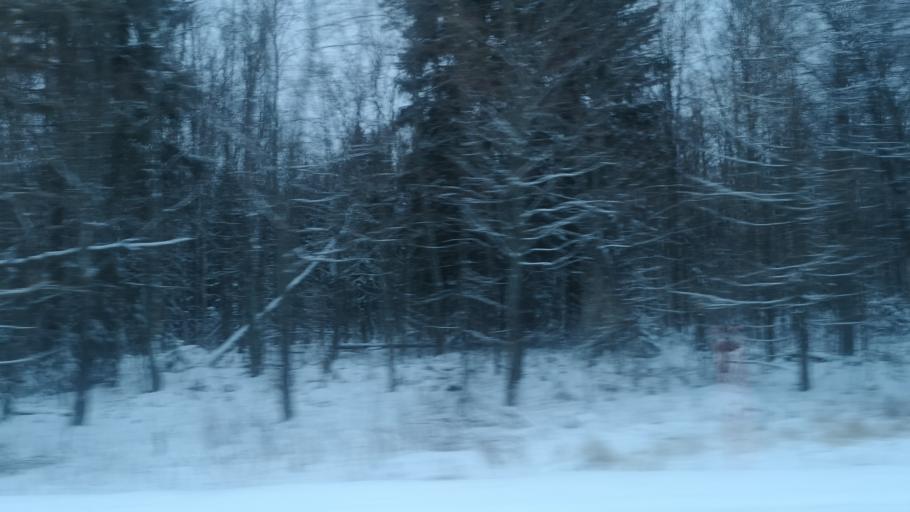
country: FI
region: Southern Savonia
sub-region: Savonlinna
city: Savonlinna
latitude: 62.0034
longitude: 28.7403
